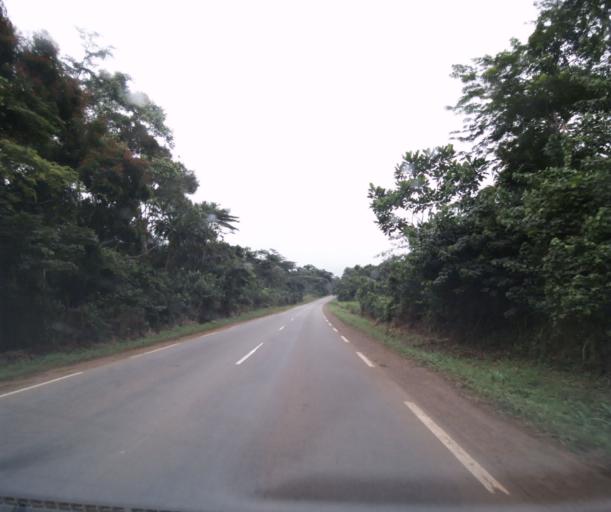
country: CM
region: Centre
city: Mbankomo
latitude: 3.7691
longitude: 11.1820
